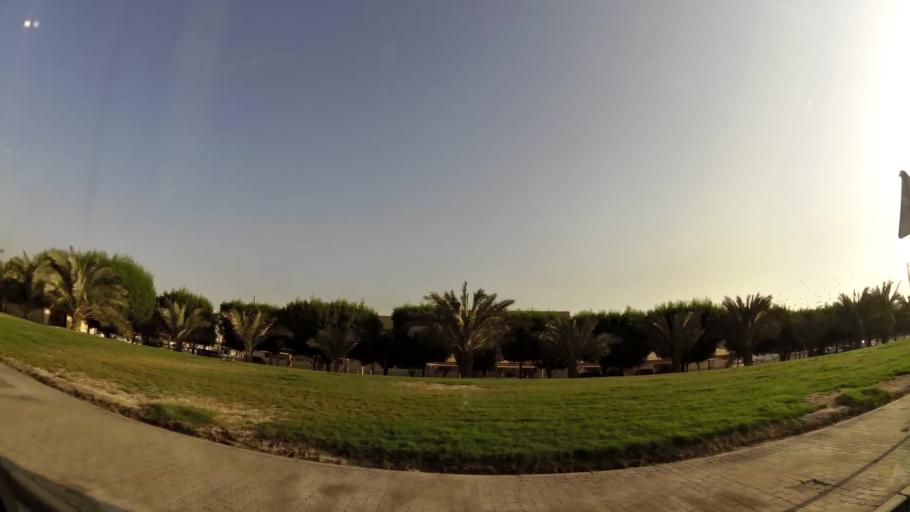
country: KW
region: Muhafazat Hawalli
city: Hawalli
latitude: 29.3405
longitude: 48.0516
